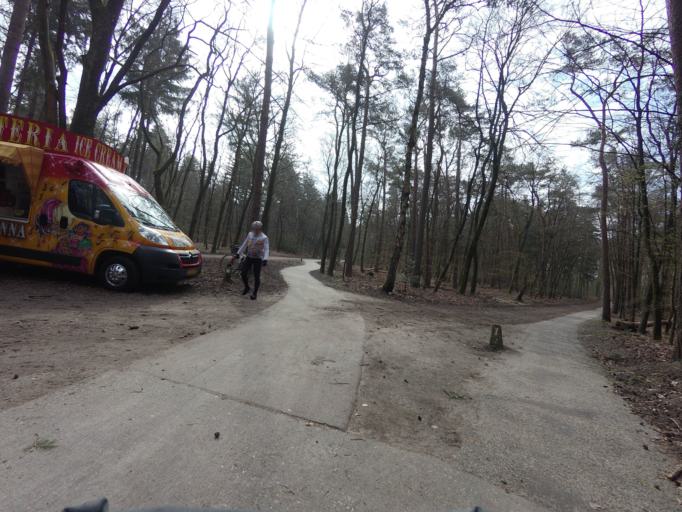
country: NL
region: Gelderland
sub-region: Gemeente Nunspeet
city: Nunspeet
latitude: 52.3407
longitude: 5.7089
